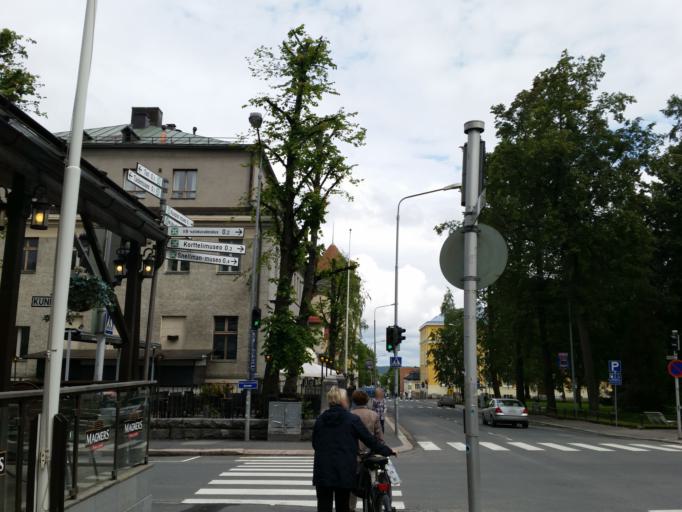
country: FI
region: Northern Savo
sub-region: Kuopio
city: Kuopio
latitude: 62.8917
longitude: 27.6843
